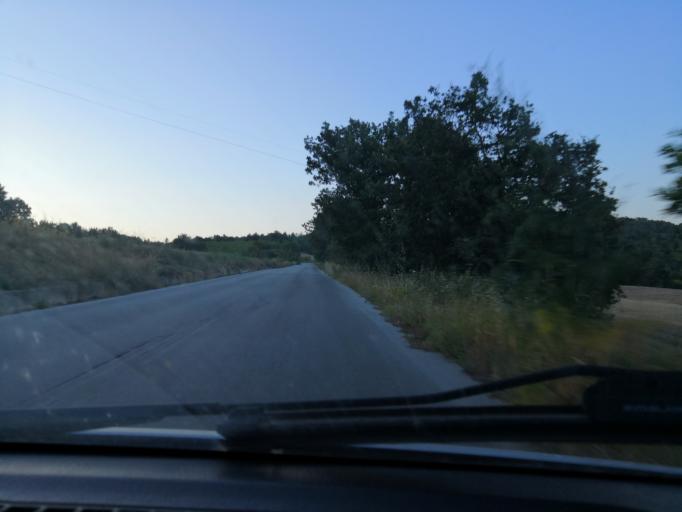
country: IT
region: Molise
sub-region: Provincia di Campobasso
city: Jelsi
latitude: 41.5111
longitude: 14.7747
